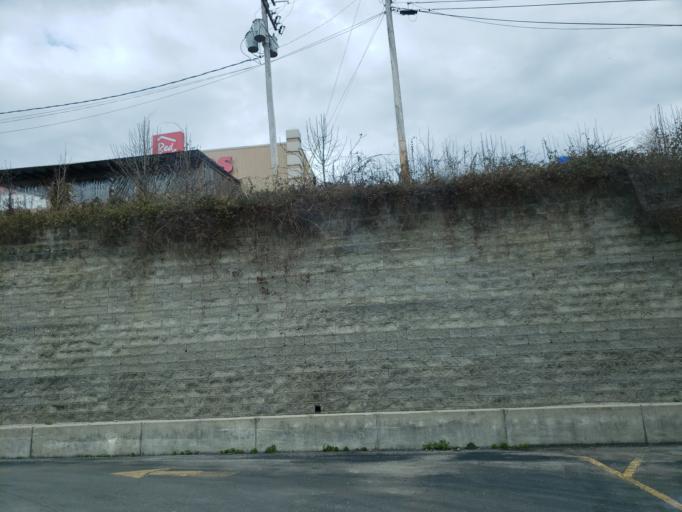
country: US
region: Kentucky
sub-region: Whitley County
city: Corbin
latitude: 36.9191
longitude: -84.1275
